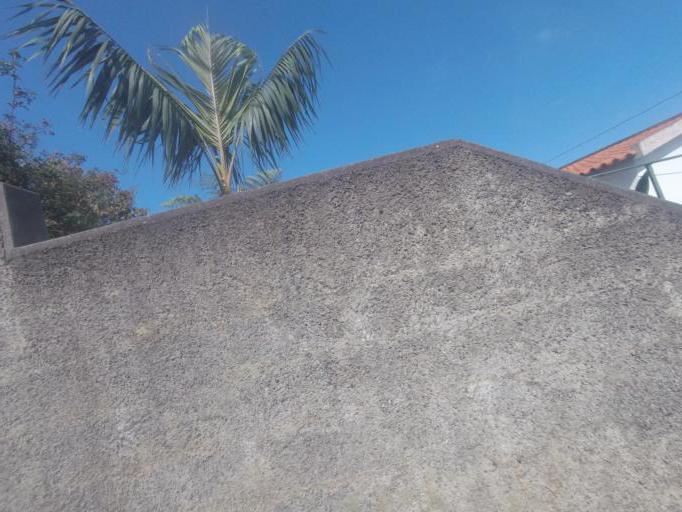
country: PT
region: Madeira
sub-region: Funchal
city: Nossa Senhora do Monte
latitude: 32.6751
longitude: -16.9457
